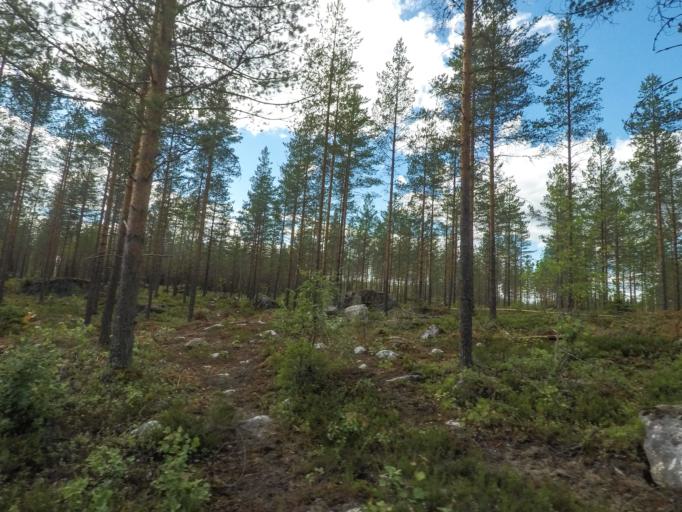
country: FI
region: Central Finland
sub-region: Jyvaeskylae
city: Hankasalmi
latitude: 62.4051
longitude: 26.6585
